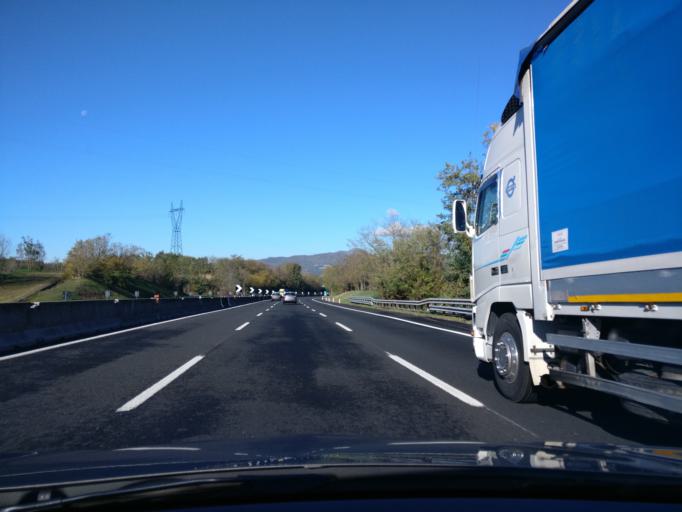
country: IT
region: Campania
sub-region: Provincia di Caserta
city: Zuni
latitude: 41.2151
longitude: 14.1047
